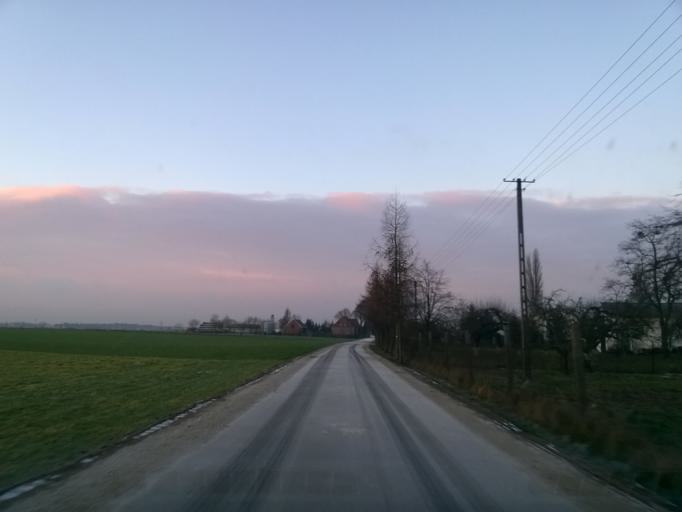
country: PL
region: Kujawsko-Pomorskie
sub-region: Powiat nakielski
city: Kcynia
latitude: 53.0141
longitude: 17.4443
